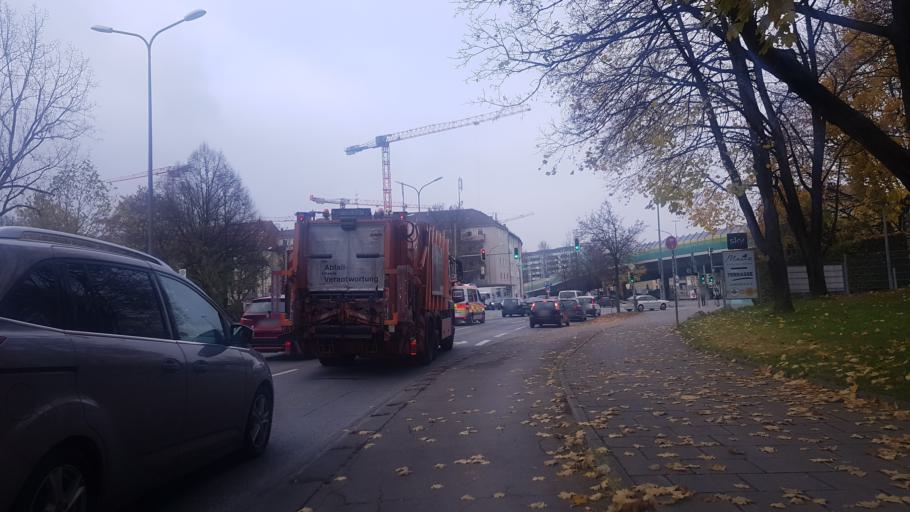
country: DE
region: Bavaria
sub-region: Upper Bavaria
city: Munich
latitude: 48.1111
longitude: 11.5706
